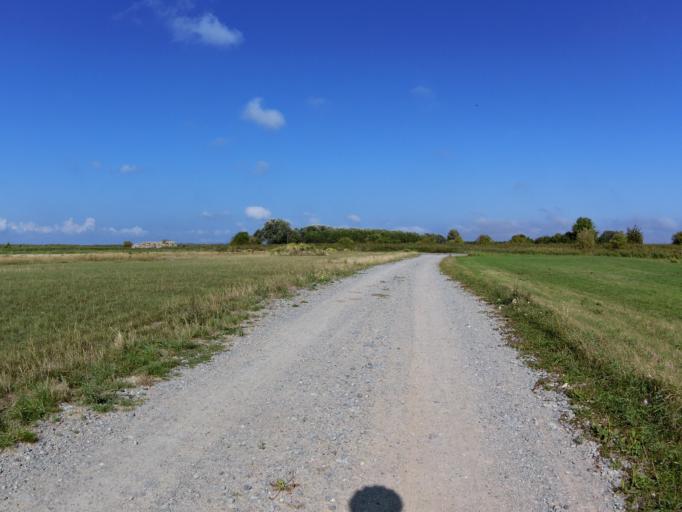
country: DE
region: Mecklenburg-Vorpommern
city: Loddin
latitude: 53.9791
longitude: 14.0516
